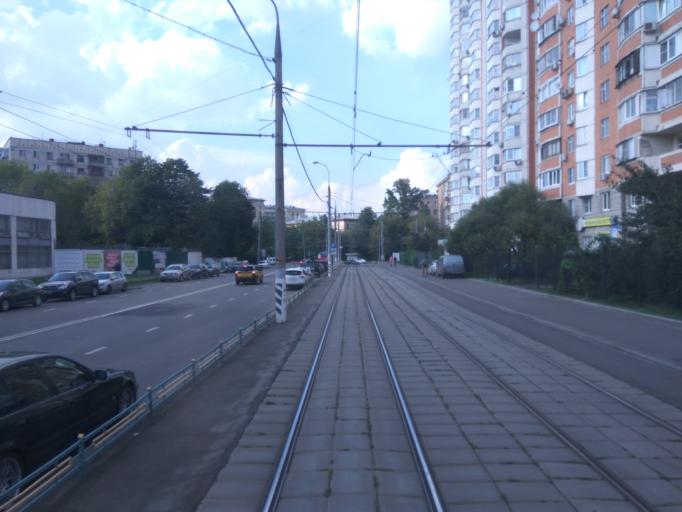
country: RU
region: Moscow
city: Lefortovo
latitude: 55.7519
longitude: 37.7127
